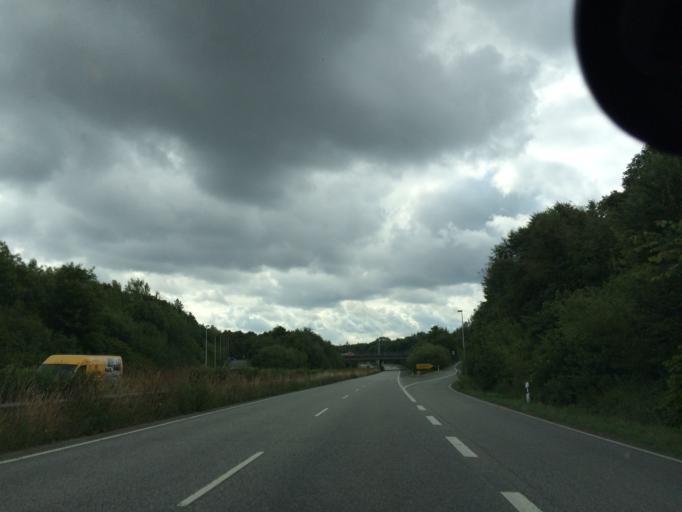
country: DE
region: Schleswig-Holstein
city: Kronshagen
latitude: 54.3595
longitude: 10.0919
